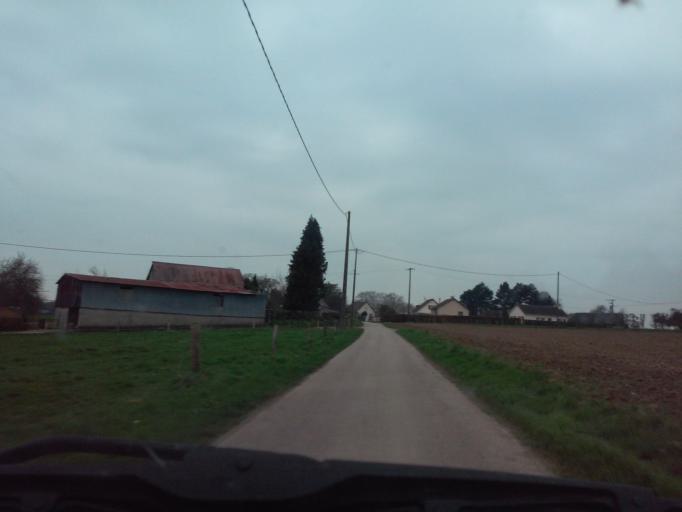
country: FR
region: Haute-Normandie
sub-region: Departement de la Seine-Maritime
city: Lanquetot
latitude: 49.5699
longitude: 0.5480
